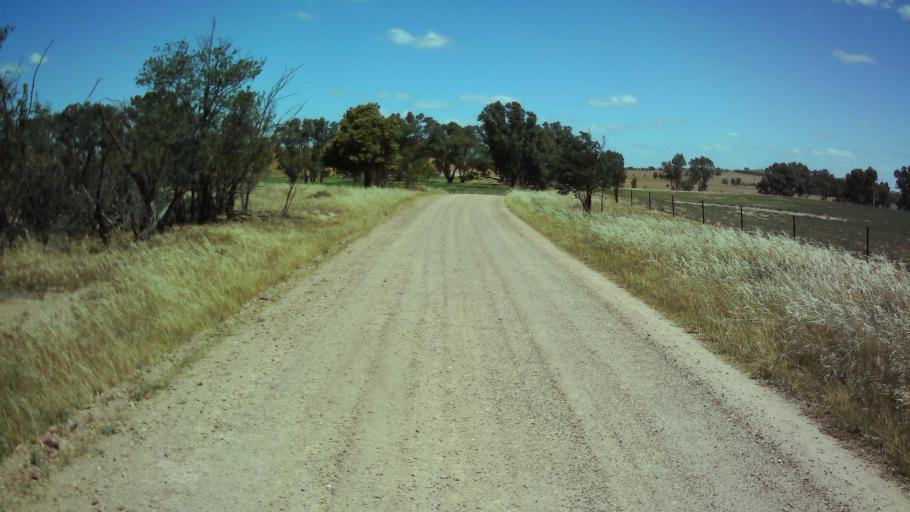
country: AU
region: New South Wales
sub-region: Weddin
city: Grenfell
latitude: -33.9351
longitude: 148.3294
